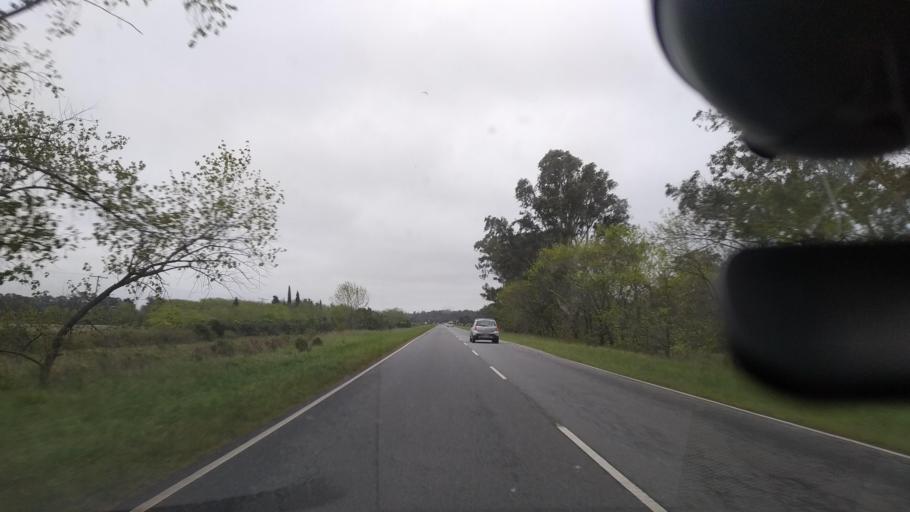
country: AR
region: Buenos Aires
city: Veronica
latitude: -35.4192
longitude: -57.3457
